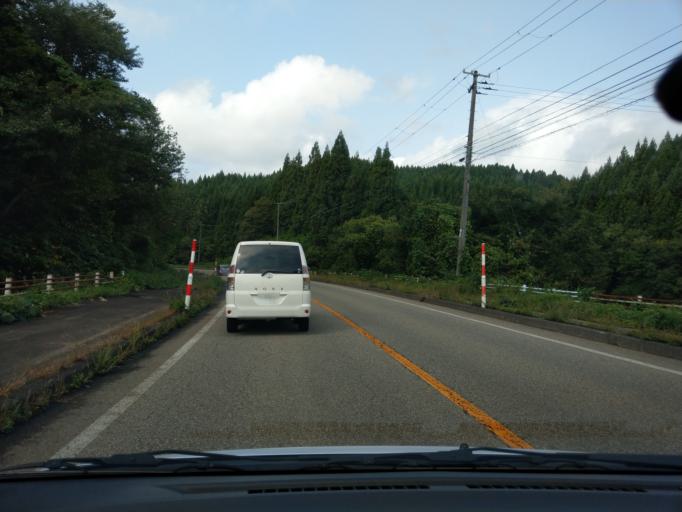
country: JP
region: Akita
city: Omagari
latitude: 39.4345
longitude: 140.3754
